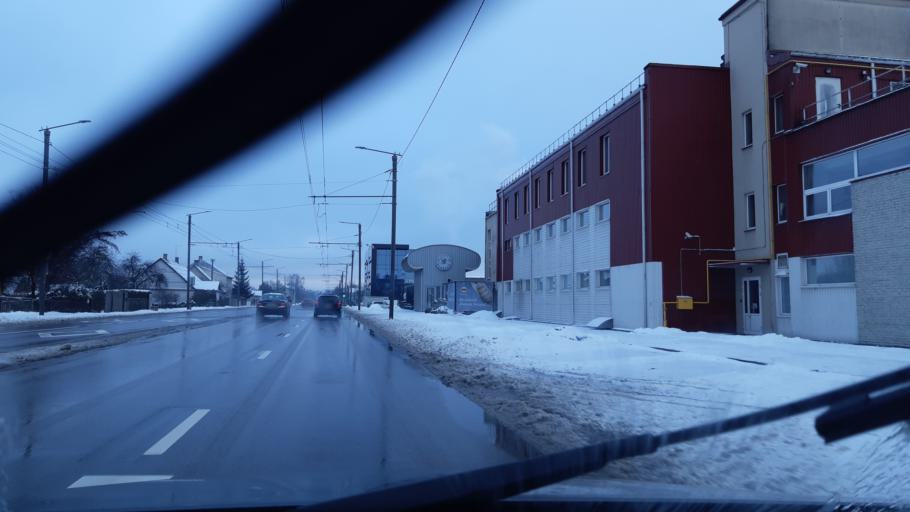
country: LT
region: Kauno apskritis
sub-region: Kauno rajonas
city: Akademija (Kaunas)
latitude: 54.9100
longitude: 23.8541
